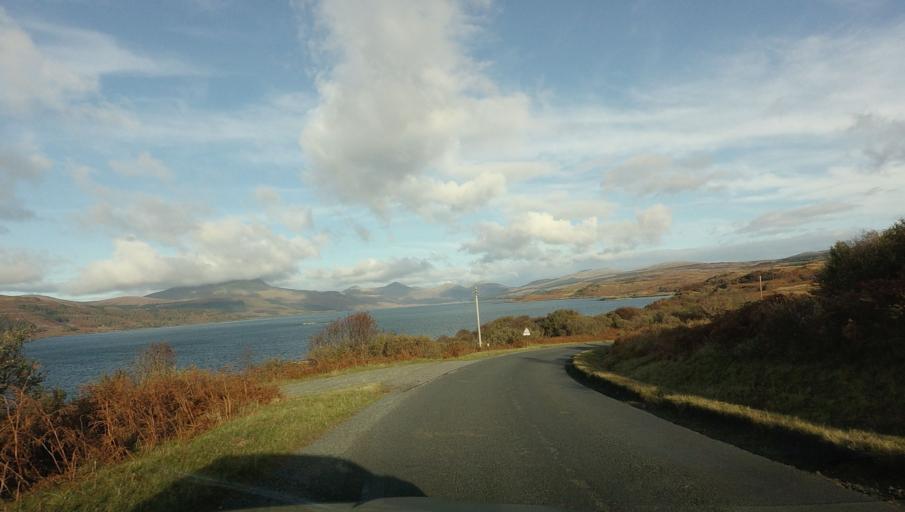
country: GB
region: Scotland
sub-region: Argyll and Bute
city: Isle Of Mull
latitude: 56.3434
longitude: -6.1219
